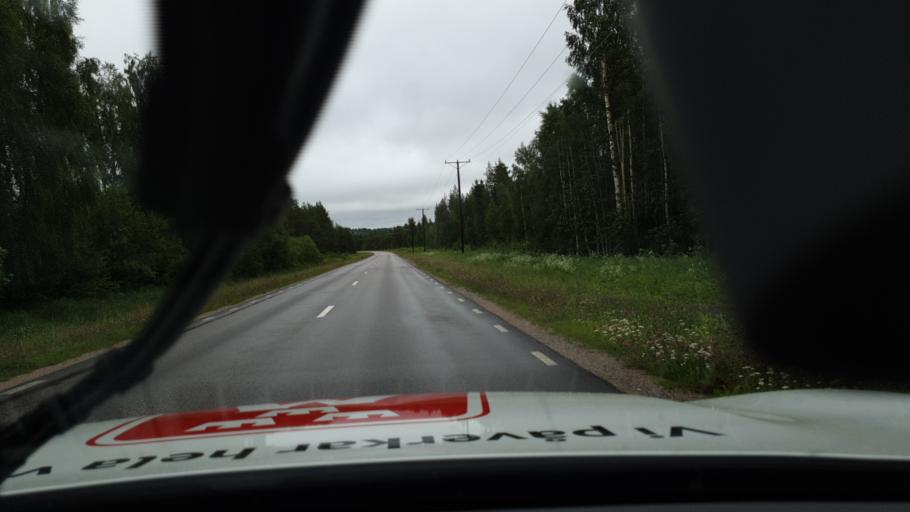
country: SE
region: Norrbotten
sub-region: Overtornea Kommun
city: OEvertornea
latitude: 66.3954
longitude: 23.5954
